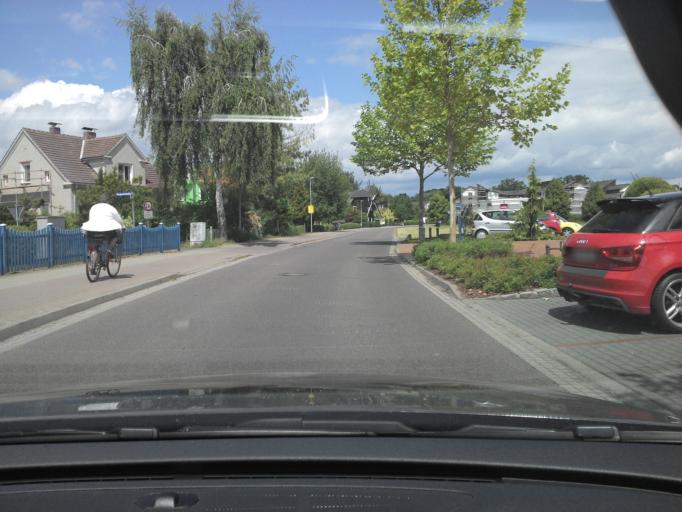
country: DE
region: Brandenburg
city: Burg
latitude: 51.8330
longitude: 14.1451
